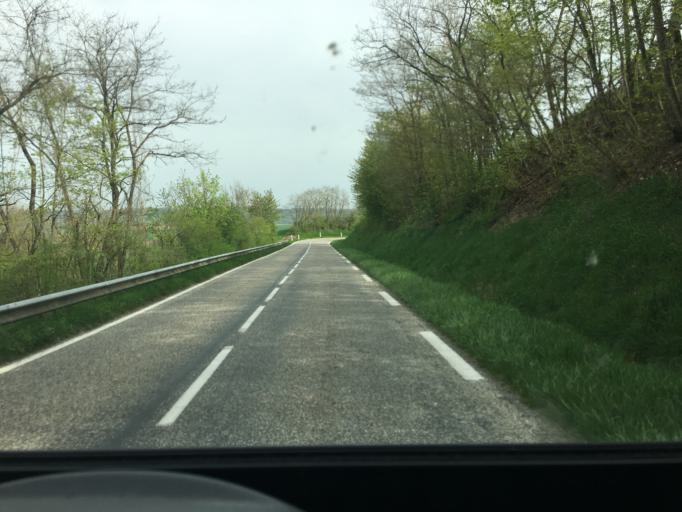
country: FR
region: Lorraine
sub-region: Departement de la Moselle
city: Vic-sur-Seille
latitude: 48.7562
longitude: 6.5458
